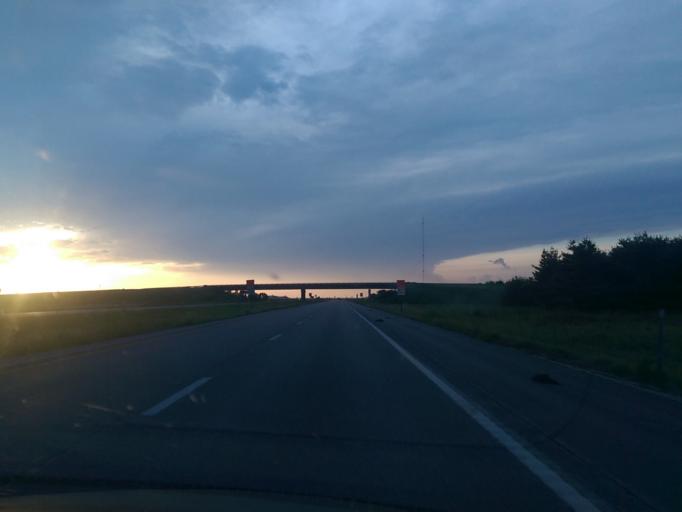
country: US
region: Missouri
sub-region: Atchison County
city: Rock Port
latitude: 40.3672
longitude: -95.5298
